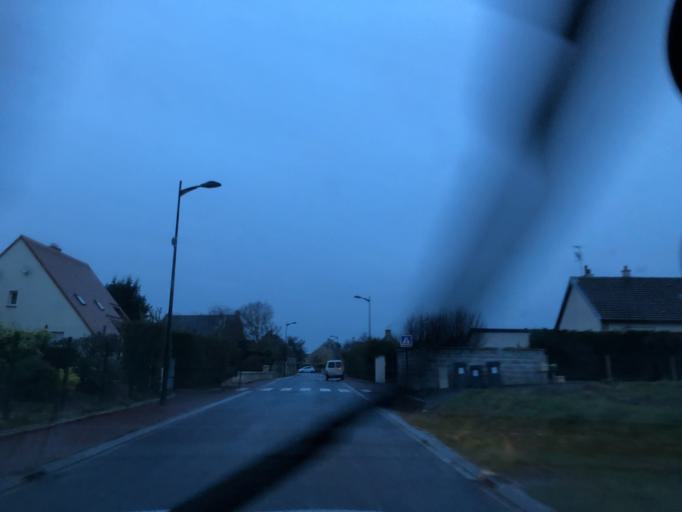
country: FR
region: Lower Normandy
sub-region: Departement du Calvados
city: Mathieu
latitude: 49.2502
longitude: -0.3637
